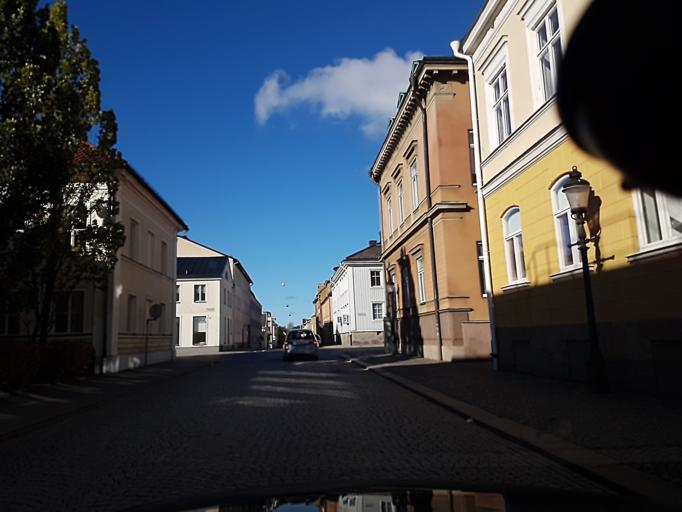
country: SE
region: Kronoberg
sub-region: Vaxjo Kommun
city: Vaexjoe
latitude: 56.8803
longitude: 14.8098
